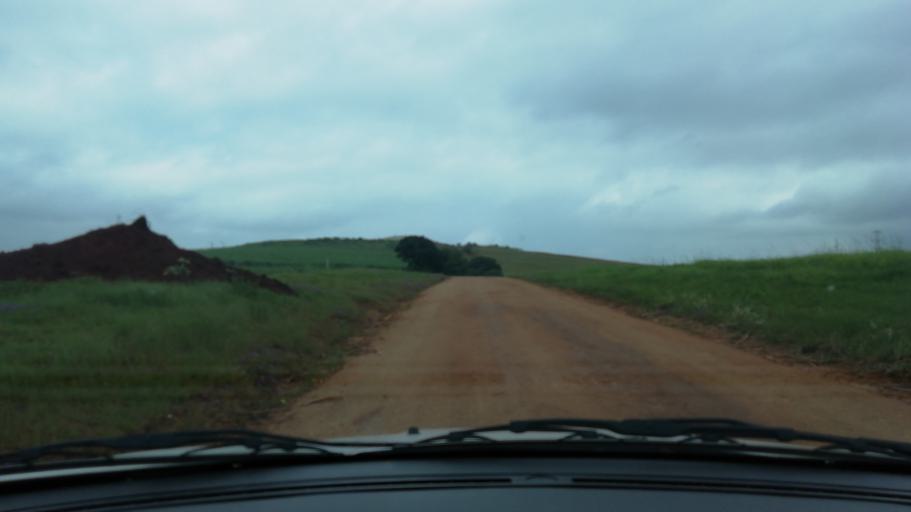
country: ZA
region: KwaZulu-Natal
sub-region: uThungulu District Municipality
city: Empangeni
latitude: -28.7305
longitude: 31.9031
